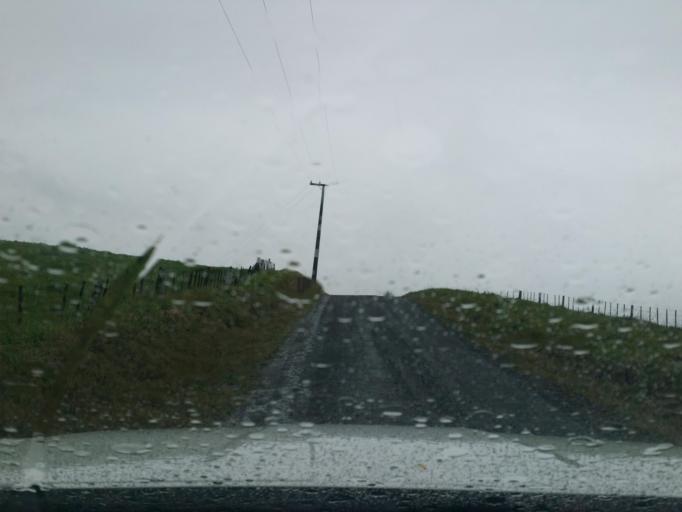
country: NZ
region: Northland
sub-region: Kaipara District
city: Dargaville
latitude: -35.8810
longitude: 173.9971
